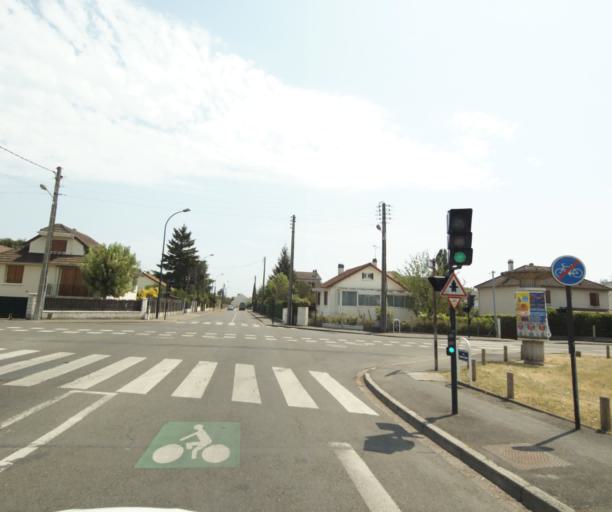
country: FR
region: Ile-de-France
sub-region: Departement des Yvelines
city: Conflans-Sainte-Honorine
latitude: 48.9994
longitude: 2.0843
